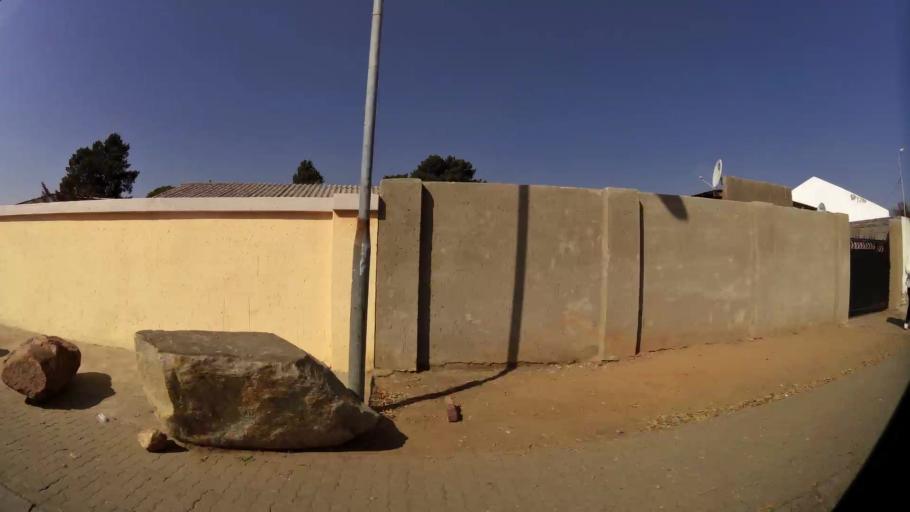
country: ZA
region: Gauteng
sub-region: City of Johannesburg Metropolitan Municipality
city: Soweto
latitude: -26.2406
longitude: 27.9410
